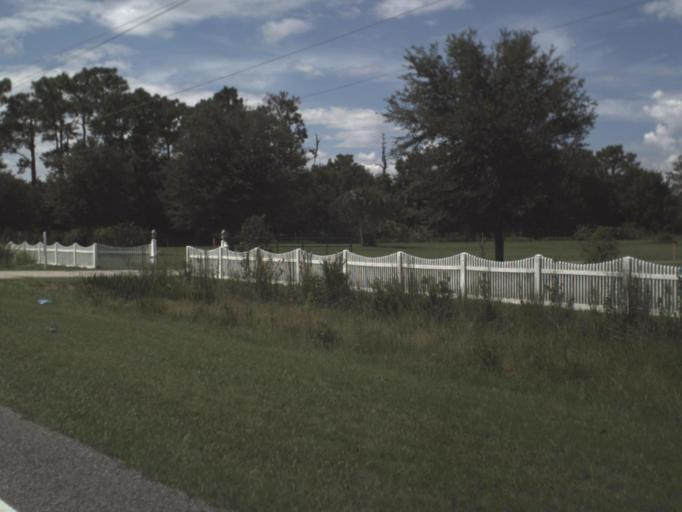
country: US
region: Florida
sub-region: Polk County
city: Babson Park
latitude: 27.8788
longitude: -81.4180
